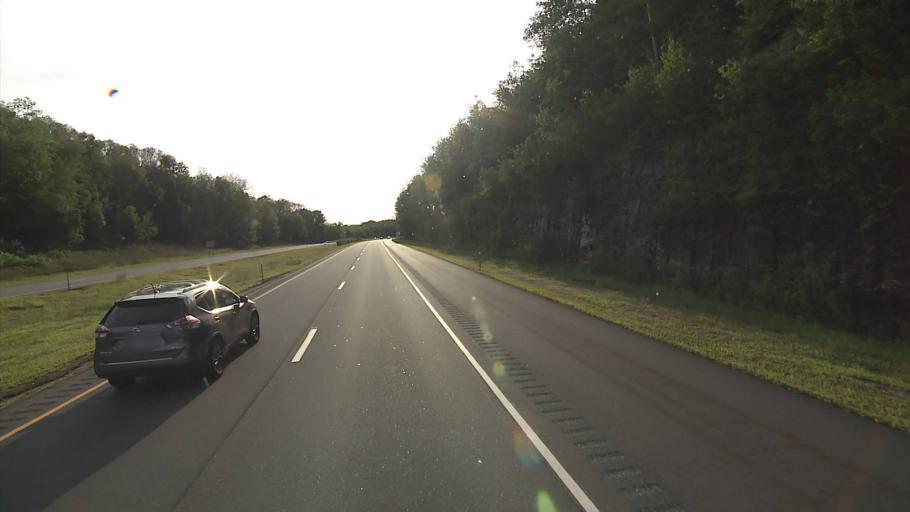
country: US
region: Connecticut
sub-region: New London County
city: Montville Center
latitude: 41.5714
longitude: -72.1976
